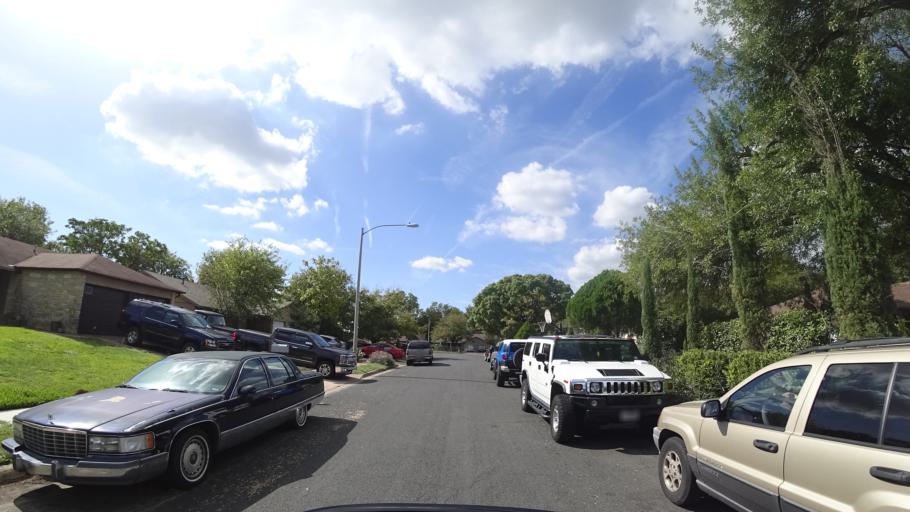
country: US
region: Texas
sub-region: Travis County
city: Onion Creek
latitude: 30.2030
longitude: -97.7951
